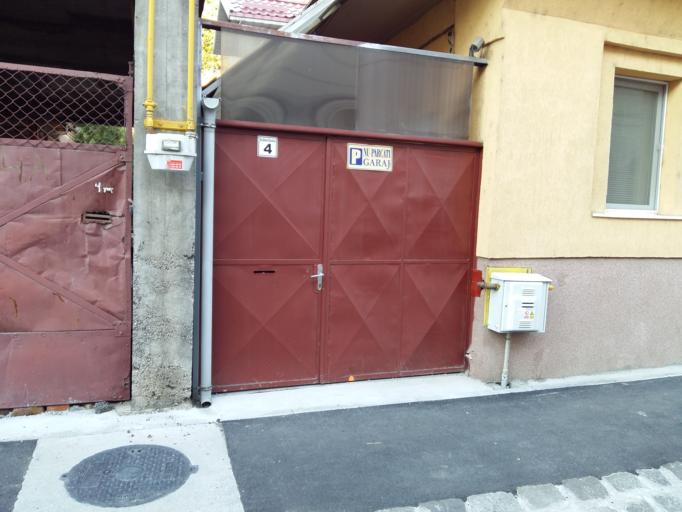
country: RO
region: Cluj
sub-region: Municipiul Cluj-Napoca
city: Cluj-Napoca
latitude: 46.7758
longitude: 23.5884
